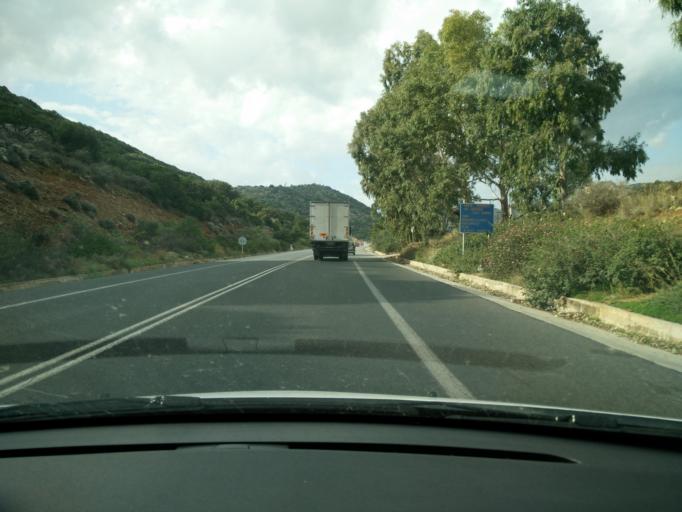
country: GR
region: Crete
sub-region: Nomos Lasithiou
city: Agios Nikolaos
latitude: 35.2027
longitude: 25.7004
